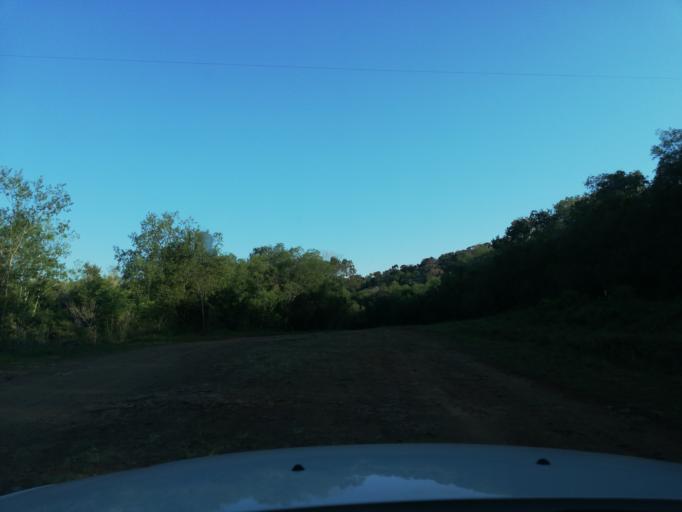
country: AR
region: Misiones
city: Cerro Cora
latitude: -27.6131
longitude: -55.7058
